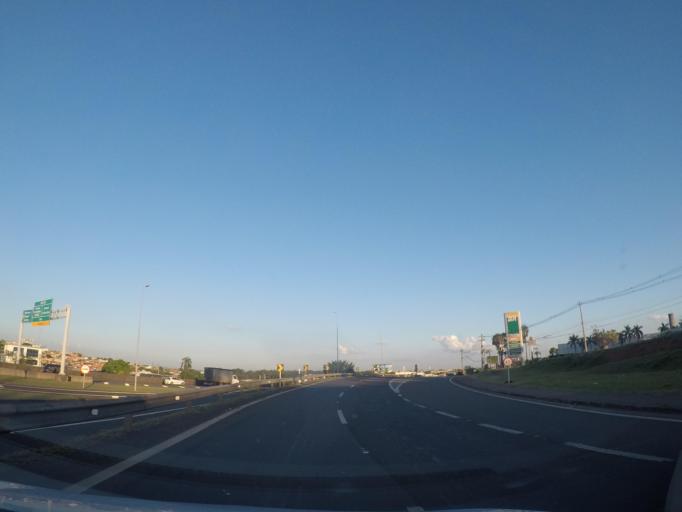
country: BR
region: Sao Paulo
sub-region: Hortolandia
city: Hortolandia
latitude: -22.8141
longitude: -47.2098
